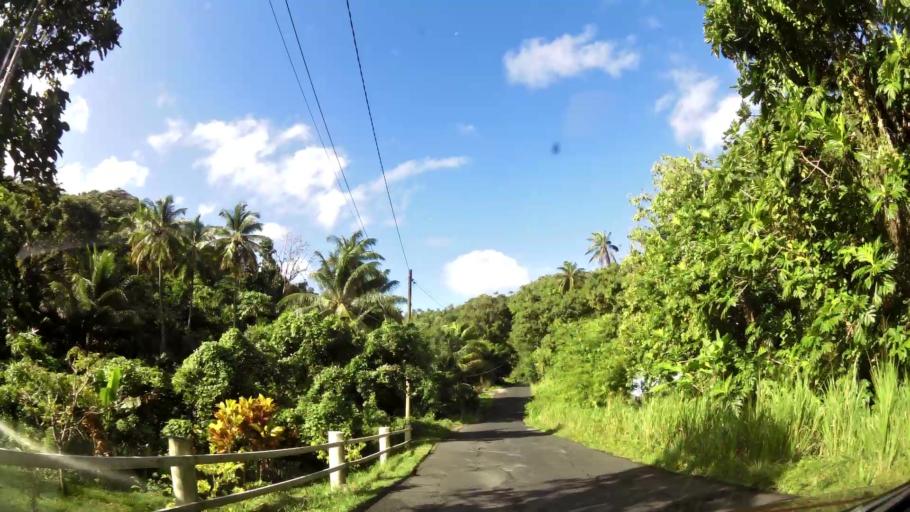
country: DM
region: Saint John
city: Portsmouth
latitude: 15.5762
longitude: -61.4277
